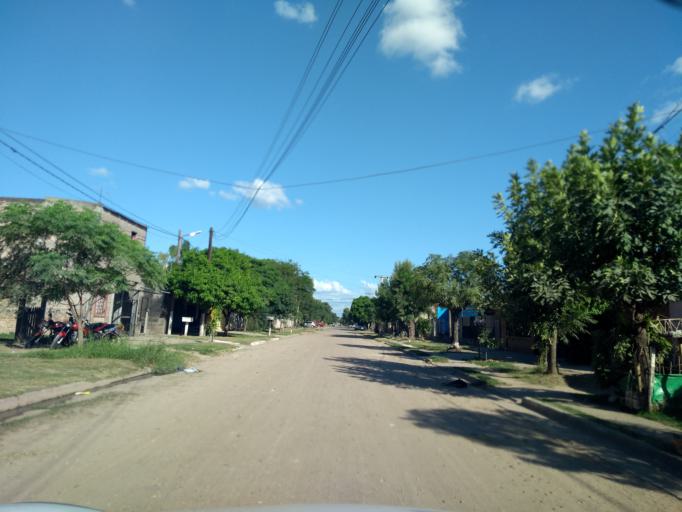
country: AR
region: Chaco
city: Resistencia
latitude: -27.4786
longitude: -58.9790
